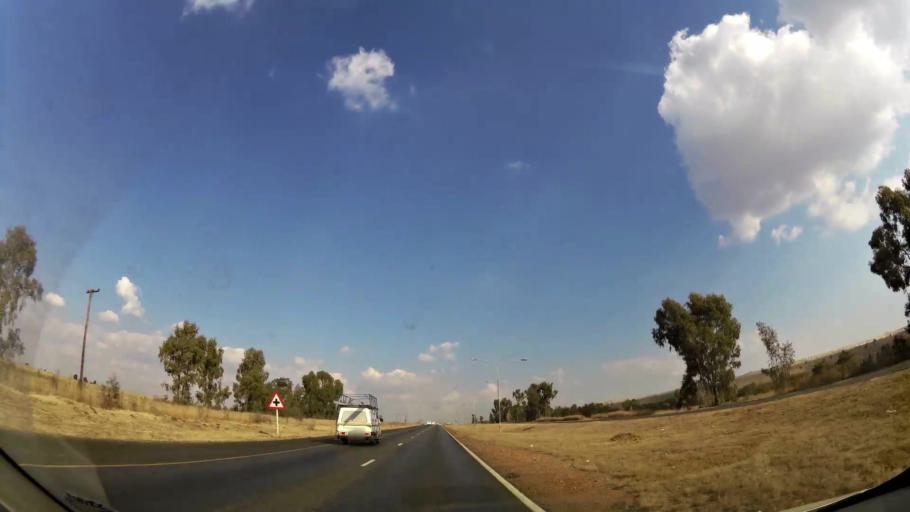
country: ZA
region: Gauteng
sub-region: Ekurhuleni Metropolitan Municipality
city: Brakpan
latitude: -26.3356
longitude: 28.3406
